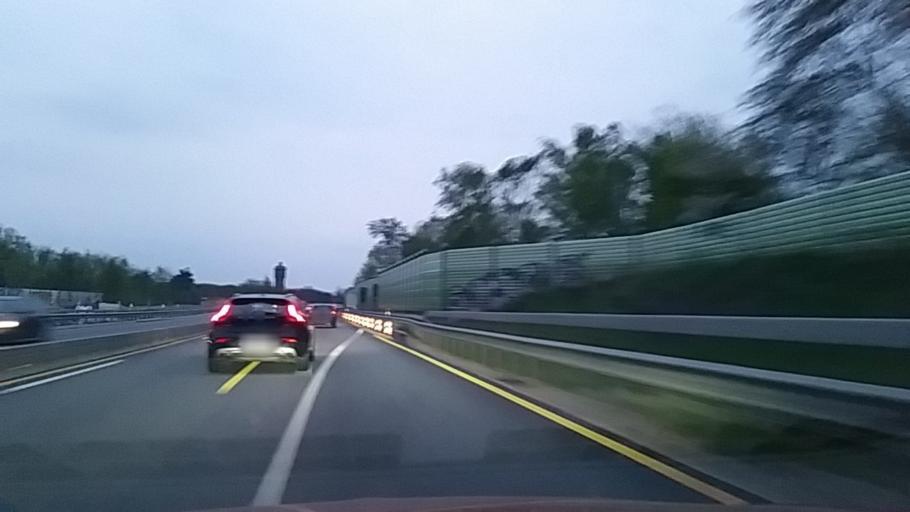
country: DE
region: Schleswig-Holstein
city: Bad Schwartau
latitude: 53.9028
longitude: 10.6837
